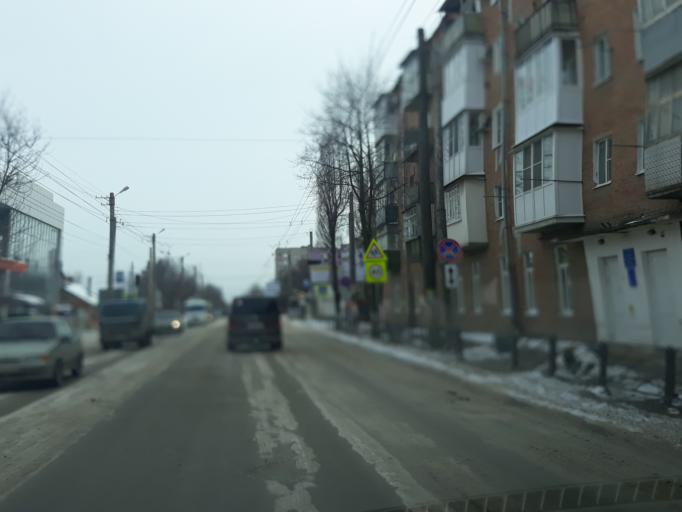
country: RU
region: Rostov
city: Taganrog
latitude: 47.2213
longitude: 38.8885
